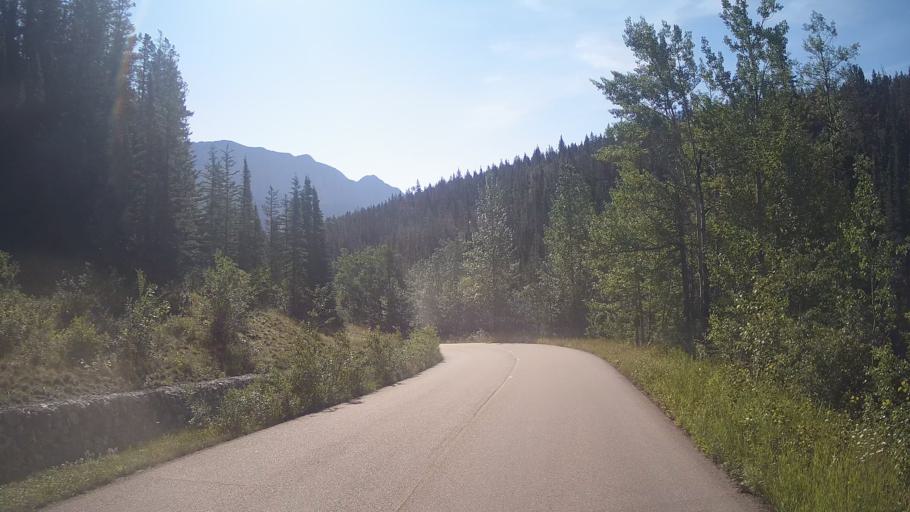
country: CA
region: Alberta
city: Hinton
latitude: 53.1769
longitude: -117.8562
